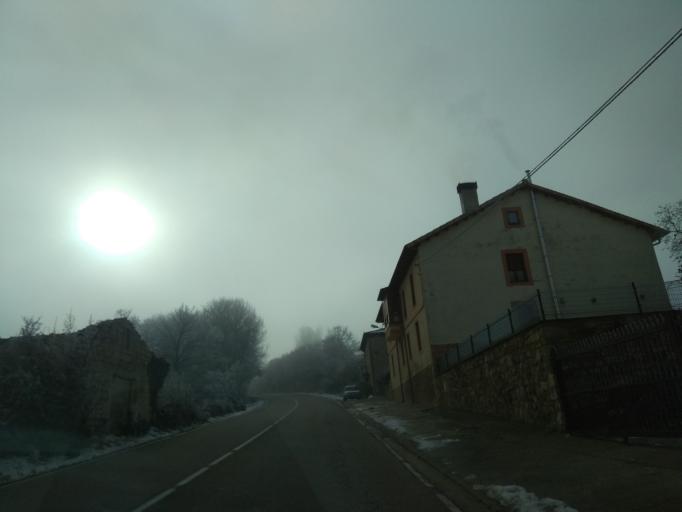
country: ES
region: Castille and Leon
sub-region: Provincia de Burgos
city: Espinosa de los Monteros
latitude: 43.0051
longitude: -3.5200
